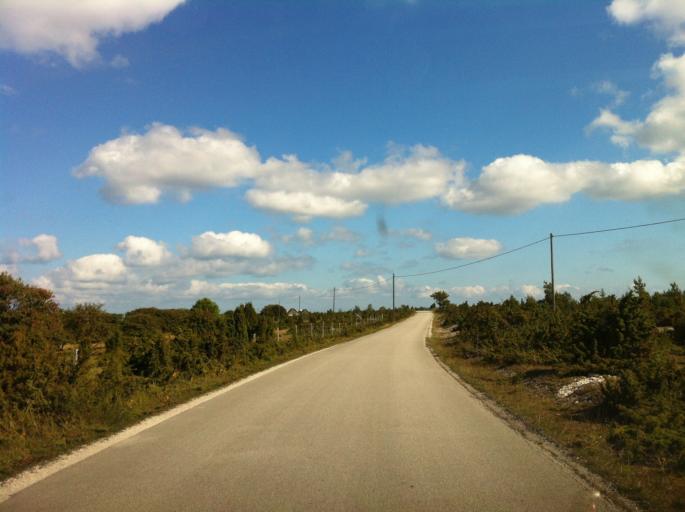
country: SE
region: Gotland
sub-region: Gotland
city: Slite
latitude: 57.9816
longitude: 19.1578
